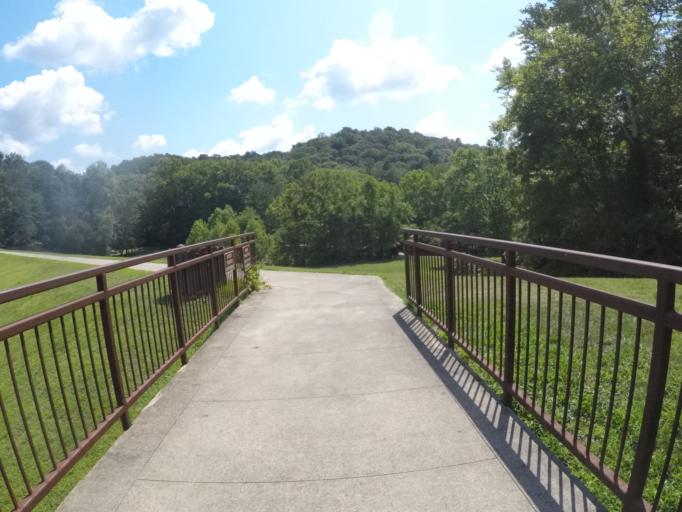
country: US
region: Ohio
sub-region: Lawrence County
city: Ironton
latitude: 38.6063
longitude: -82.6317
